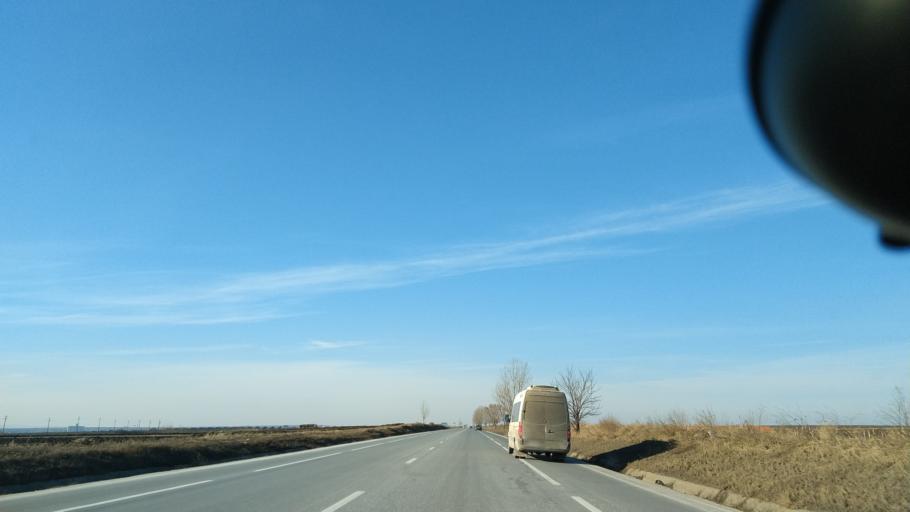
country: RO
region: Iasi
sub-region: Comuna Podu Iloaiei
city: Budai
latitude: 47.2196
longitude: 27.2054
